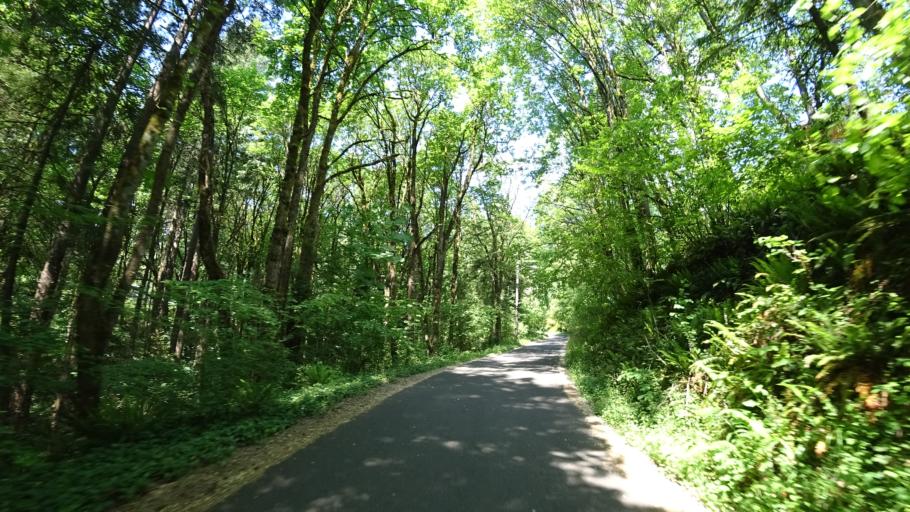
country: US
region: Oregon
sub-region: Washington County
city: West Haven-Sylvan
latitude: 45.5210
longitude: -122.7239
